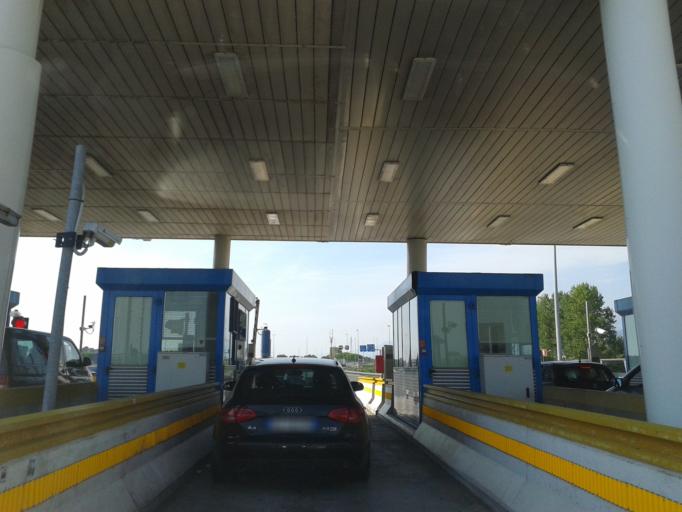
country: IT
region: Tuscany
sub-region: Provincia di Lucca
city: Camaiore
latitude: 43.8930
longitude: 10.2602
